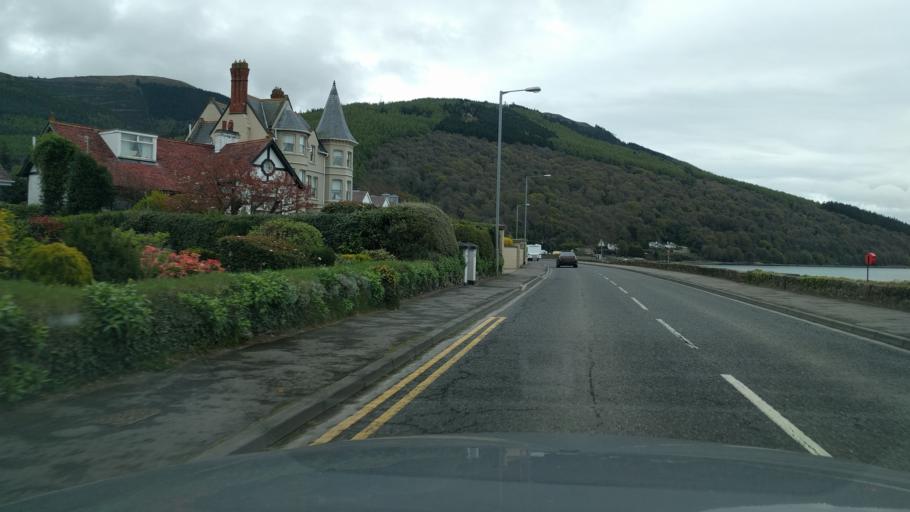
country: GB
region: Northern Ireland
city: Rostrevor
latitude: 54.0972
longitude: -6.1971
